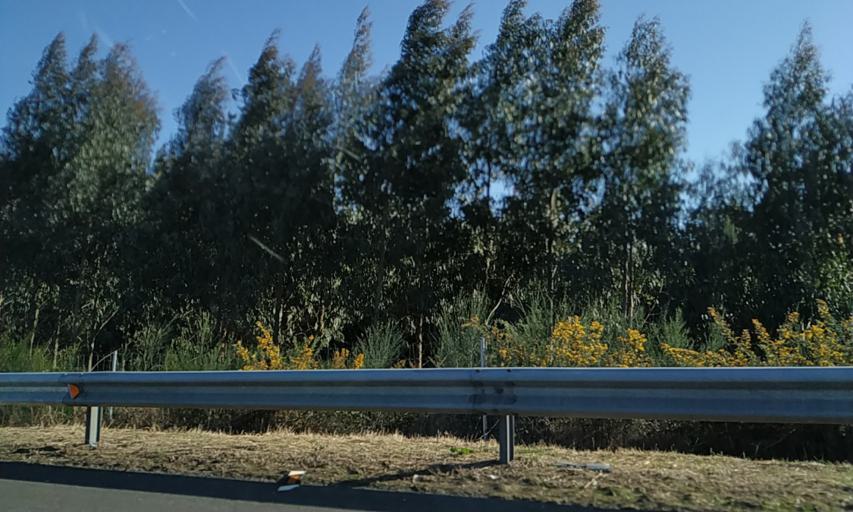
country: ES
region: Galicia
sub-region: Provincia da Coruna
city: Coiros
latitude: 43.2387
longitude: -8.1232
